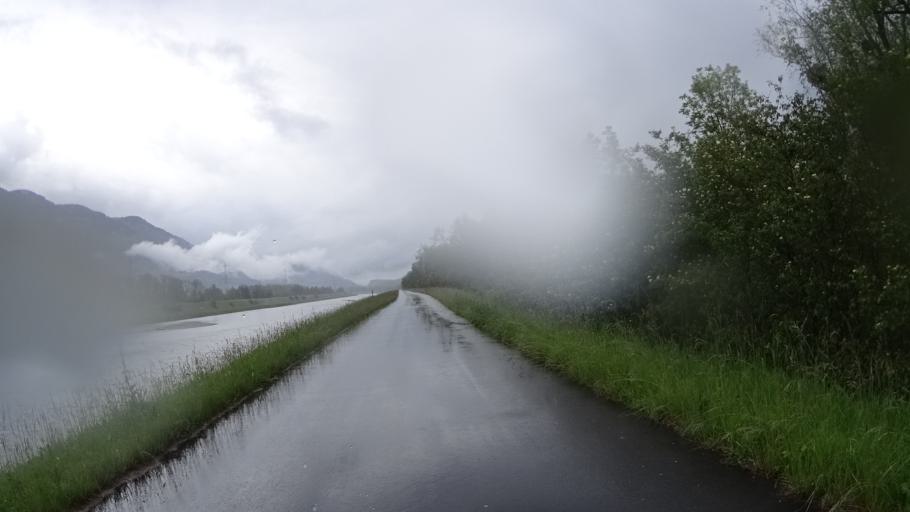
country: LI
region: Ruggell
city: Ruggell
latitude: 47.2491
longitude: 9.5242
